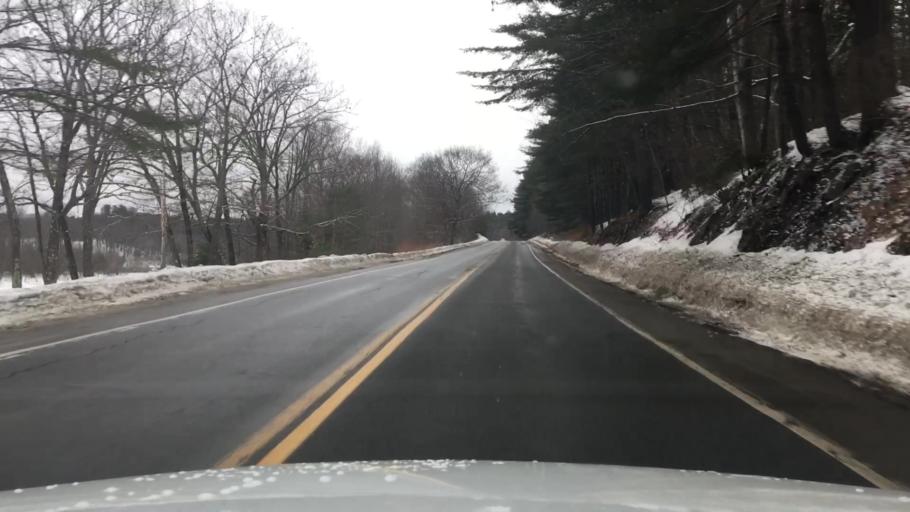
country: US
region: Maine
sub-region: Somerset County
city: Skowhegan
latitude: 44.7695
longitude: -69.6997
